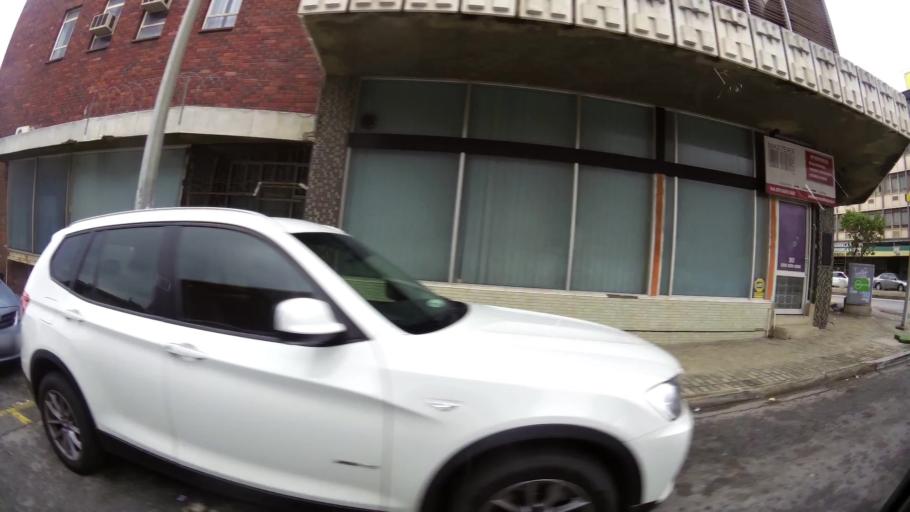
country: ZA
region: Eastern Cape
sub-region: Nelson Mandela Bay Metropolitan Municipality
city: Port Elizabeth
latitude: -33.9539
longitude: 25.6117
